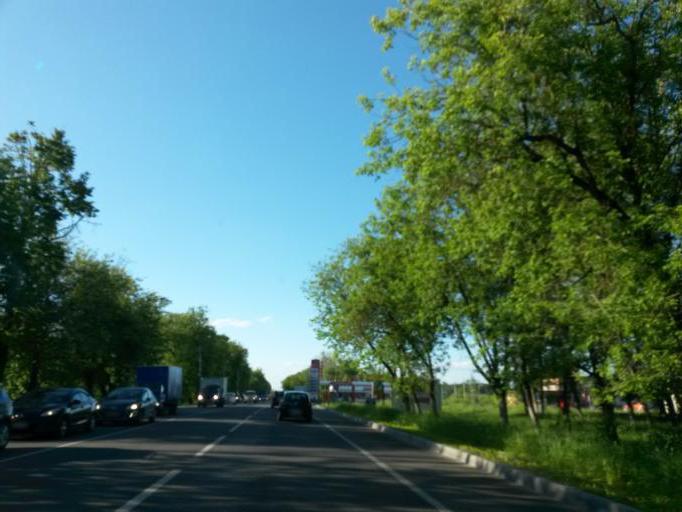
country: RU
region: Moskovskaya
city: L'vovskiy
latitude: 55.3149
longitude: 37.5288
